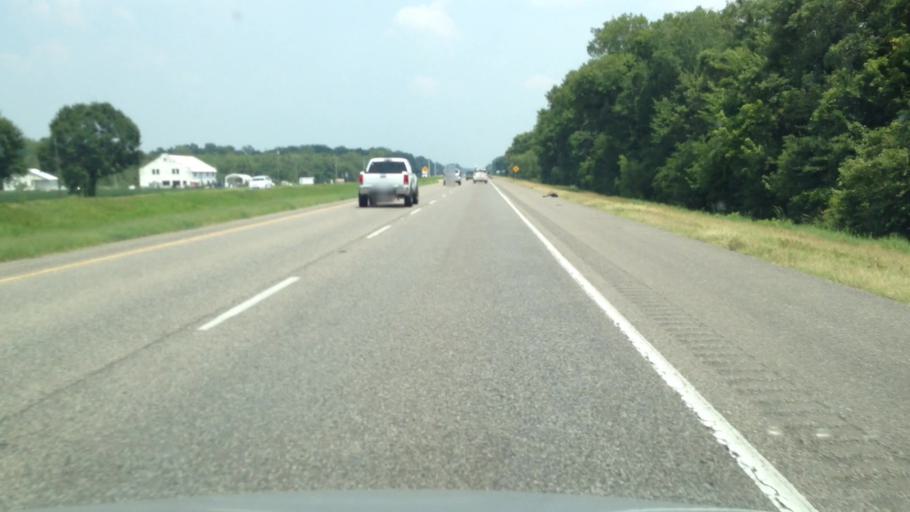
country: US
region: Louisiana
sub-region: West Baton Rouge Parish
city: Erwinville
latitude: 30.5197
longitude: -91.3680
